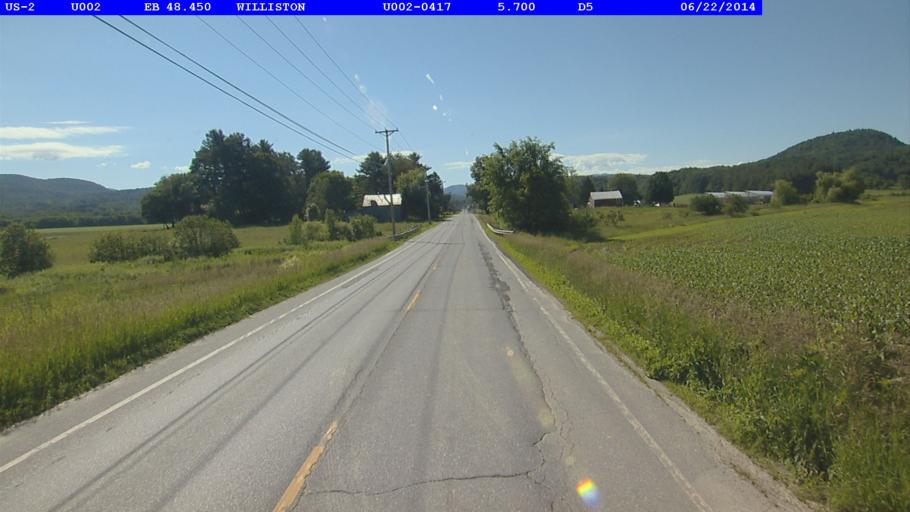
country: US
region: Vermont
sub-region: Chittenden County
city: Williston
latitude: 44.4309
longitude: -73.0315
